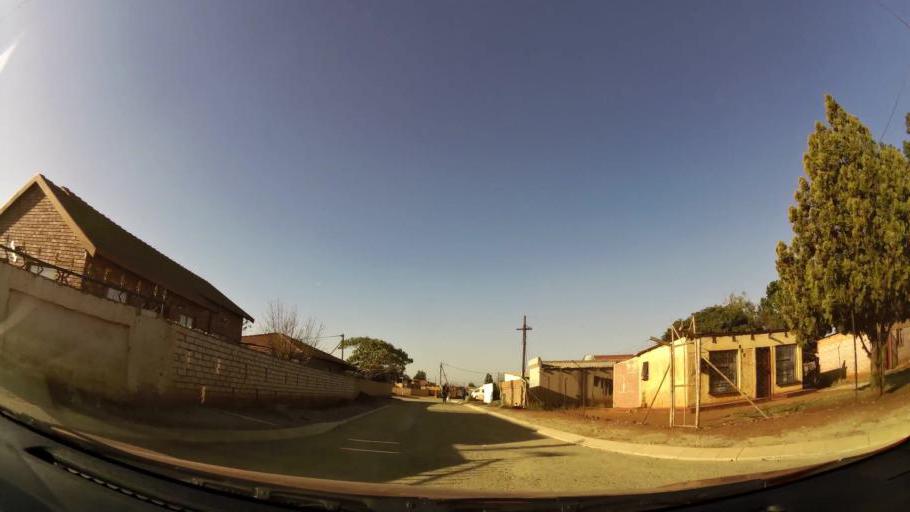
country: ZA
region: Gauteng
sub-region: City of Tshwane Metropolitan Municipality
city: Mabopane
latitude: -25.5918
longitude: 28.1004
